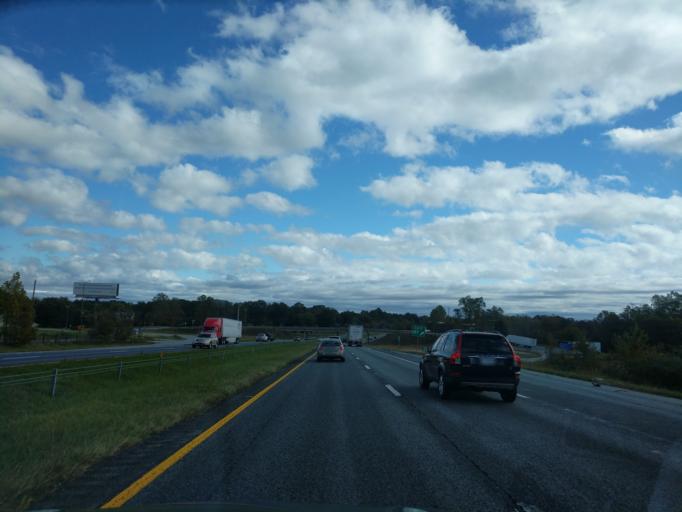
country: US
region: South Carolina
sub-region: Spartanburg County
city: Cowpens
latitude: 35.0697
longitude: -81.7639
